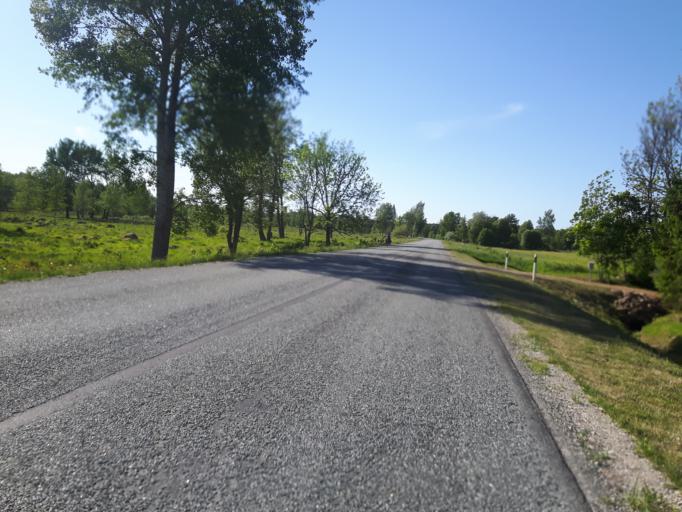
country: EE
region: Laeaene-Virumaa
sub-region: Kadrina vald
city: Kadrina
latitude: 59.5369
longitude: 26.0469
